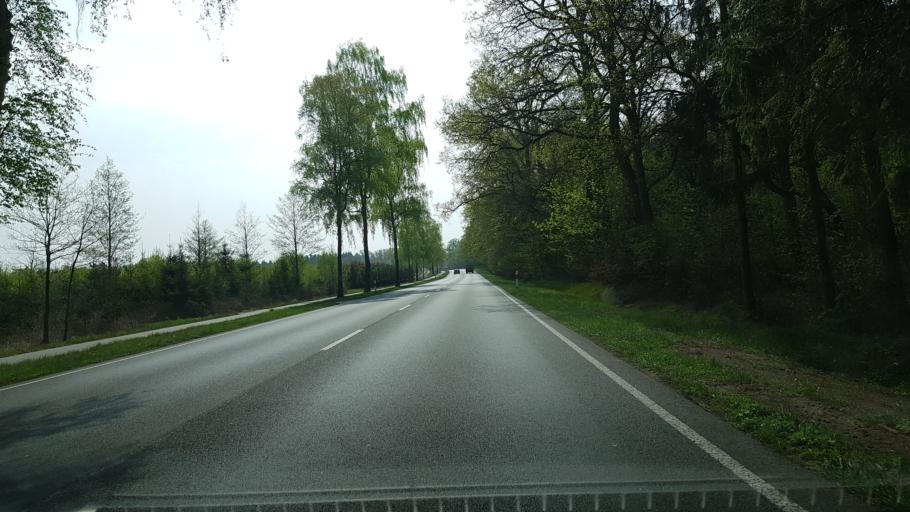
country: DE
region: Lower Saxony
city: Soltau
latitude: 52.9625
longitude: 9.8581
